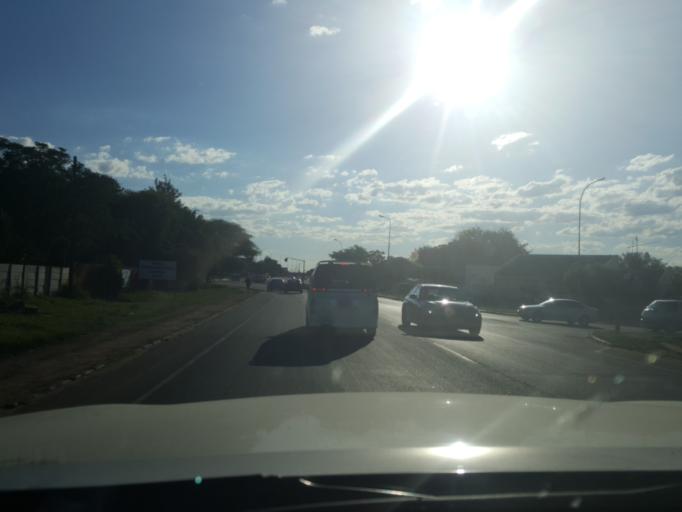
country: BW
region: South East
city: Gaborone
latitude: -24.6445
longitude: 25.9312
